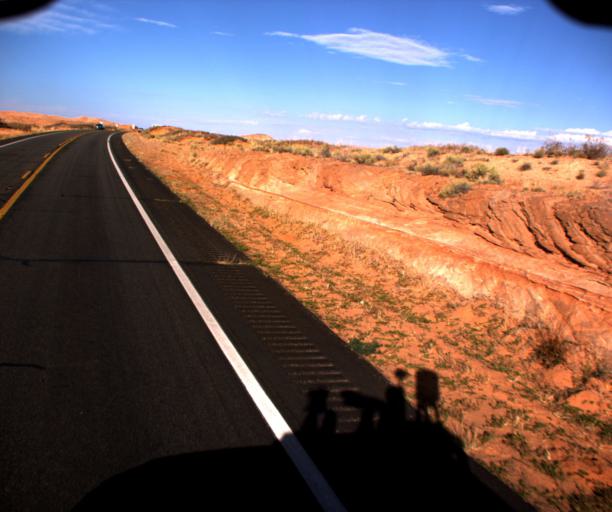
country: US
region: Arizona
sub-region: Apache County
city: Many Farms
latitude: 36.9240
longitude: -109.6094
